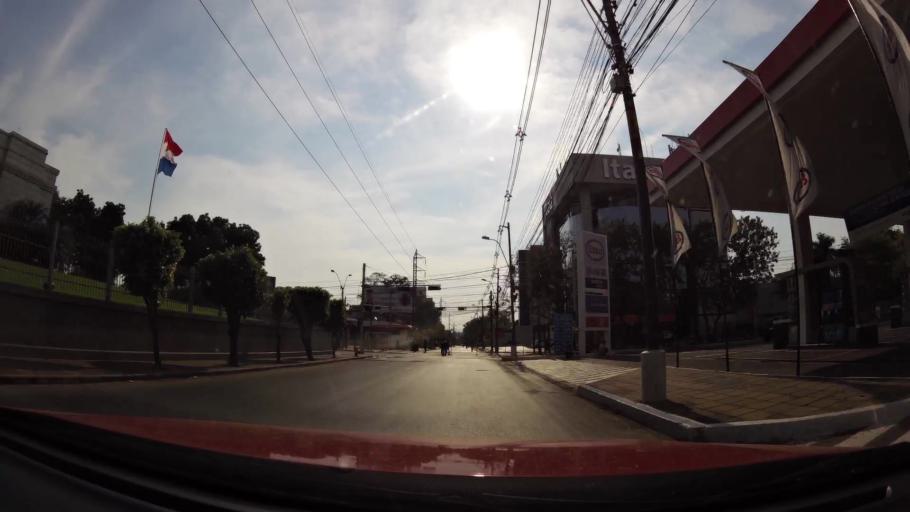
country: PY
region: Asuncion
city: Asuncion
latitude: -25.2882
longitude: -57.6027
